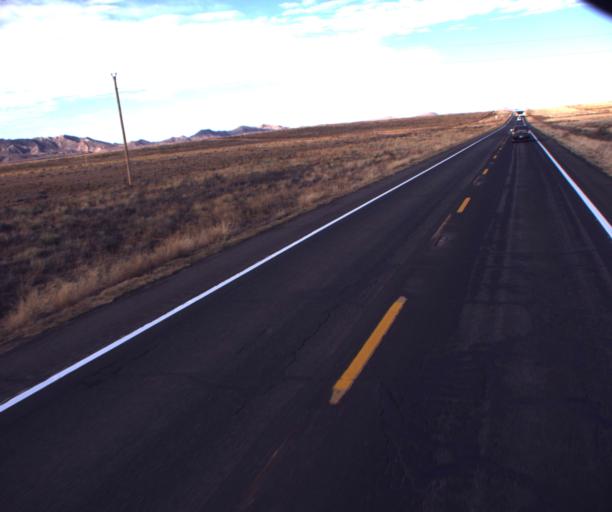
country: US
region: Arizona
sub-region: Apache County
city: Lukachukai
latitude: 36.9612
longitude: -109.3921
